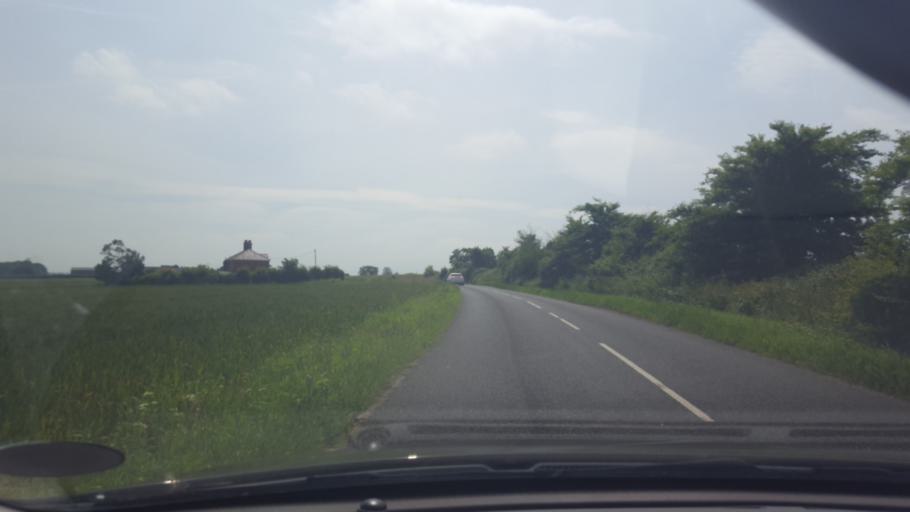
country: GB
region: England
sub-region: Essex
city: Little Clacton
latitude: 51.8211
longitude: 1.1835
